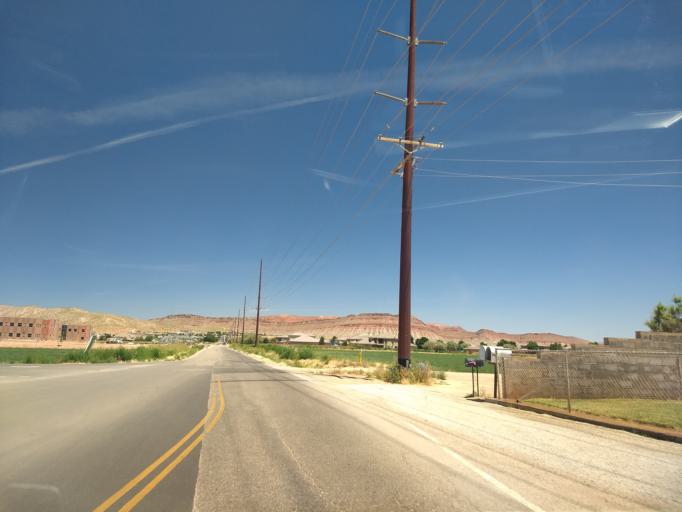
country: US
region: Utah
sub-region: Washington County
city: Washington
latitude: 37.0887
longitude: -113.5183
